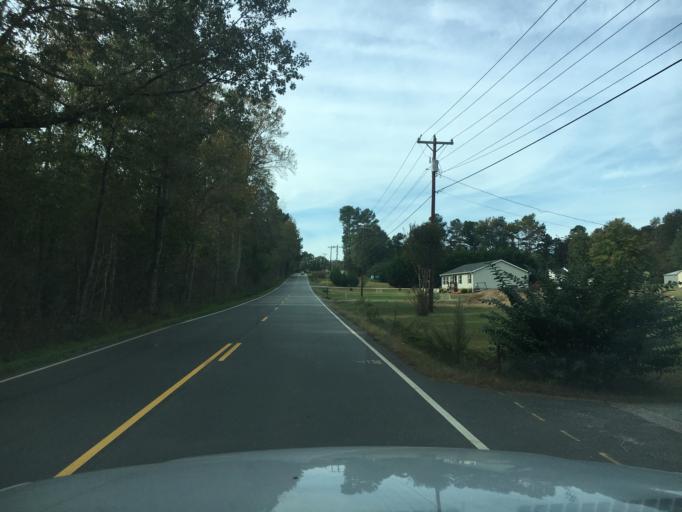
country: US
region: South Carolina
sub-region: Spartanburg County
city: Duncan
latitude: 34.8869
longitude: -82.1312
